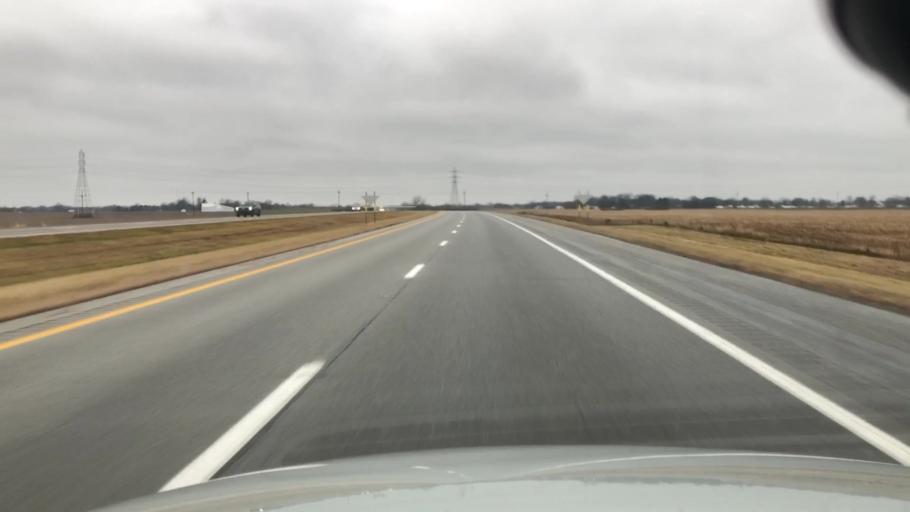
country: US
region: Ohio
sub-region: Allen County
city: Elida
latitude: 40.8350
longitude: -84.1694
